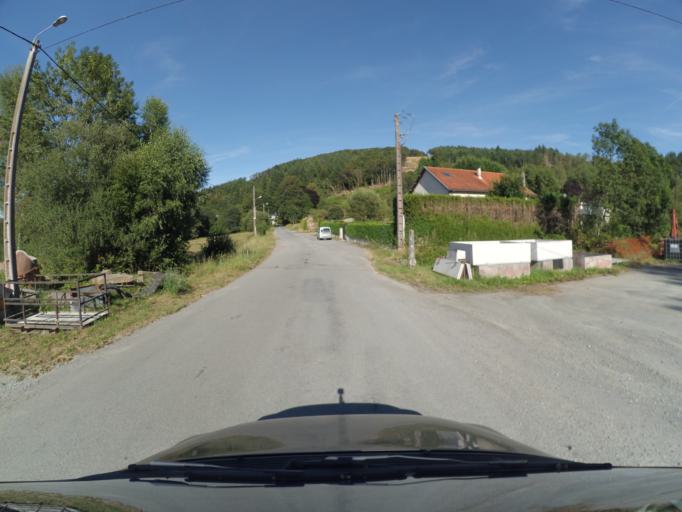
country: FR
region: Limousin
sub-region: Departement de la Correze
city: Bugeat
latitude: 45.6813
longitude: 1.9526
